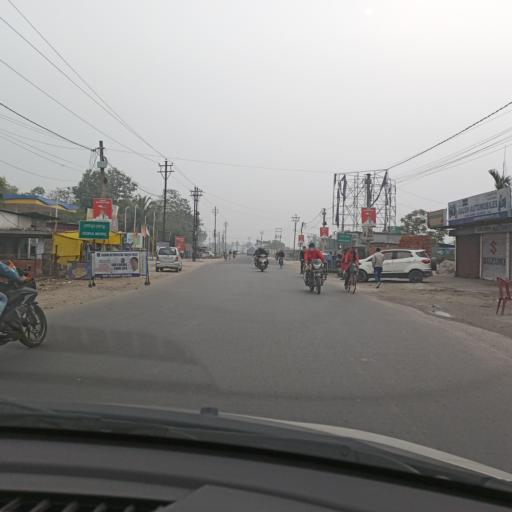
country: IN
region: West Bengal
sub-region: Darjiling
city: Shiliguri
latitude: 26.6770
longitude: 88.4622
